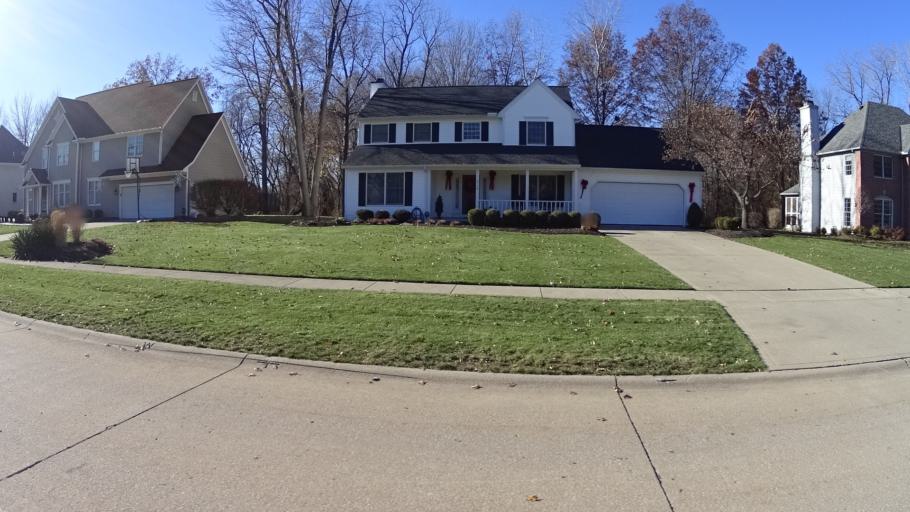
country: US
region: Ohio
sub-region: Lorain County
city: Avon
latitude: 41.4579
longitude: -82.0288
